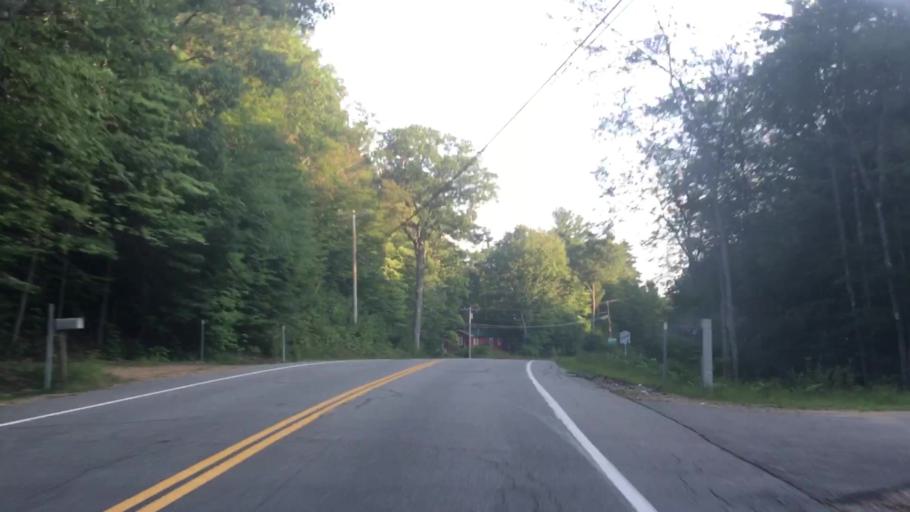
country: US
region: New Hampshire
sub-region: Belknap County
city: Gilmanton
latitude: 43.4583
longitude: -71.4212
